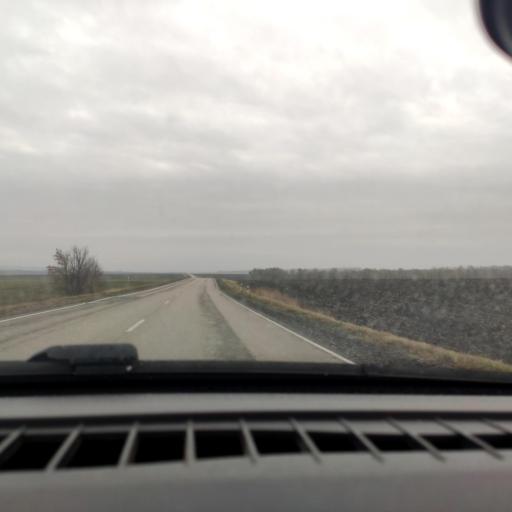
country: RU
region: Belgorod
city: Ilovka
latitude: 50.7786
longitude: 38.8084
